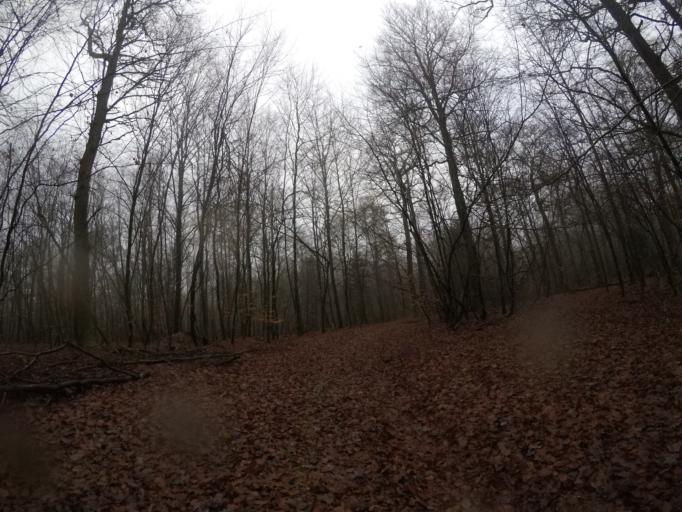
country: BE
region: Wallonia
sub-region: Province du Luxembourg
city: Fauvillers
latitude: 49.8114
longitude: 5.6182
